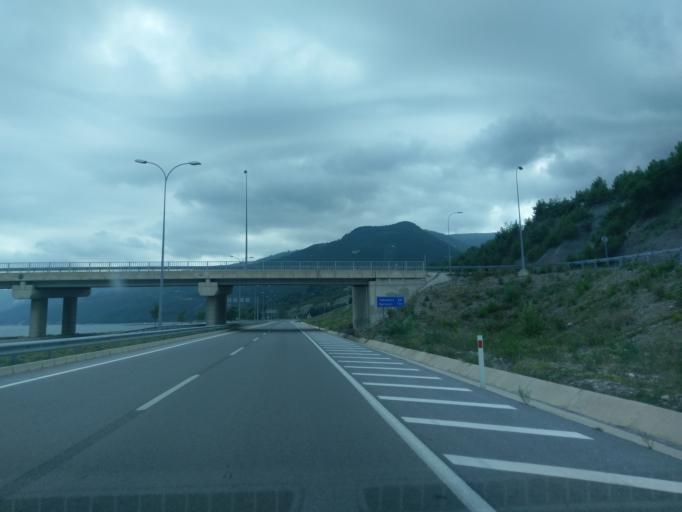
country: TR
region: Sinop
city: Dikmen
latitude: 41.7274
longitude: 35.2636
